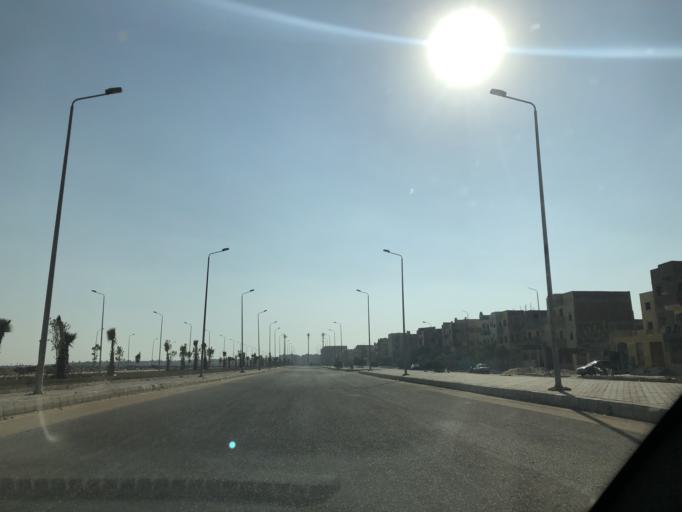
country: EG
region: Al Jizah
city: Madinat Sittah Uktubar
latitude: 29.9247
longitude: 31.0670
